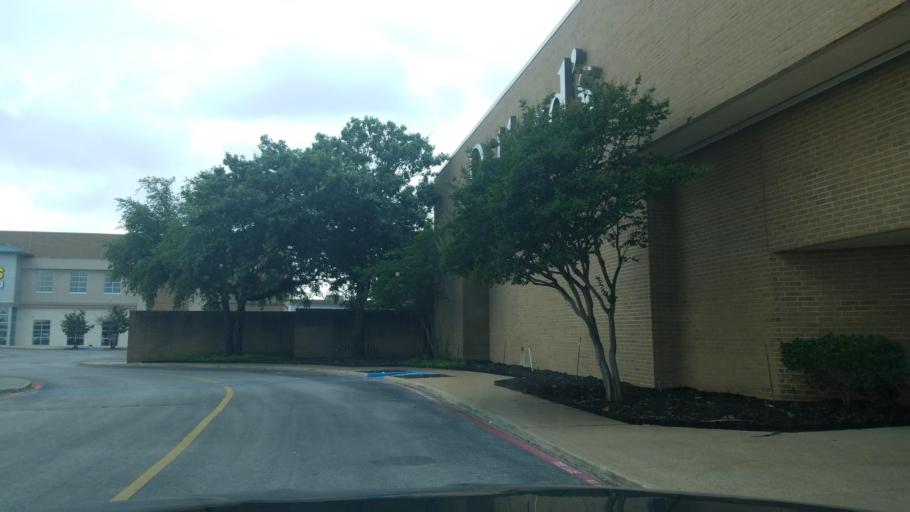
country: US
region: Texas
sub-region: Denton County
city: Denton
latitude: 33.1919
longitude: -97.1074
